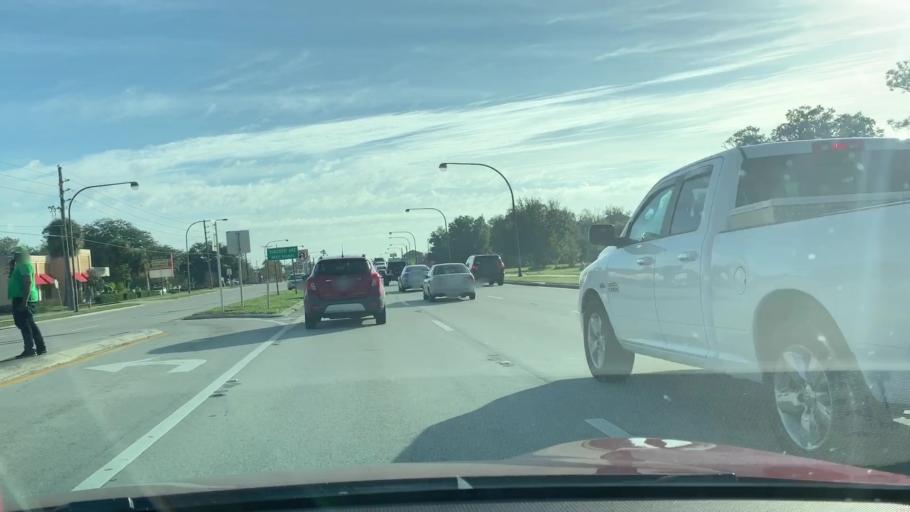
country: US
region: Florida
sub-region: Osceola County
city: Kissimmee
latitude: 28.3045
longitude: -81.4276
